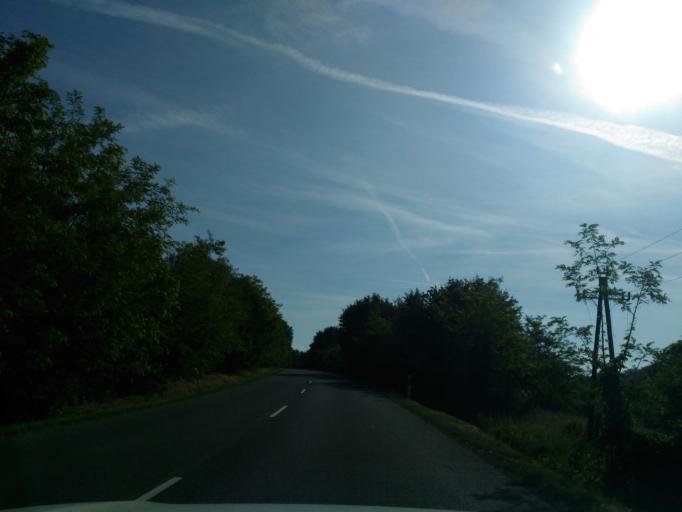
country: HU
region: Baranya
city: Hosszuheteny
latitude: 46.1842
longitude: 18.3112
